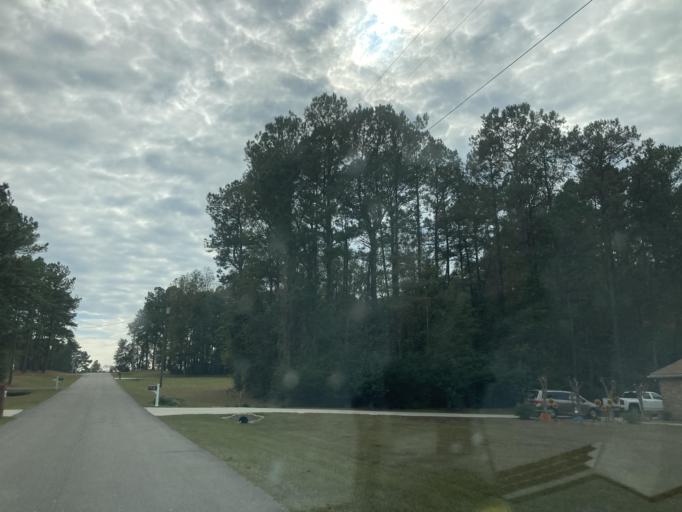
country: US
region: Mississippi
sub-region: Lamar County
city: West Hattiesburg
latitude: 31.2761
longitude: -89.4451
